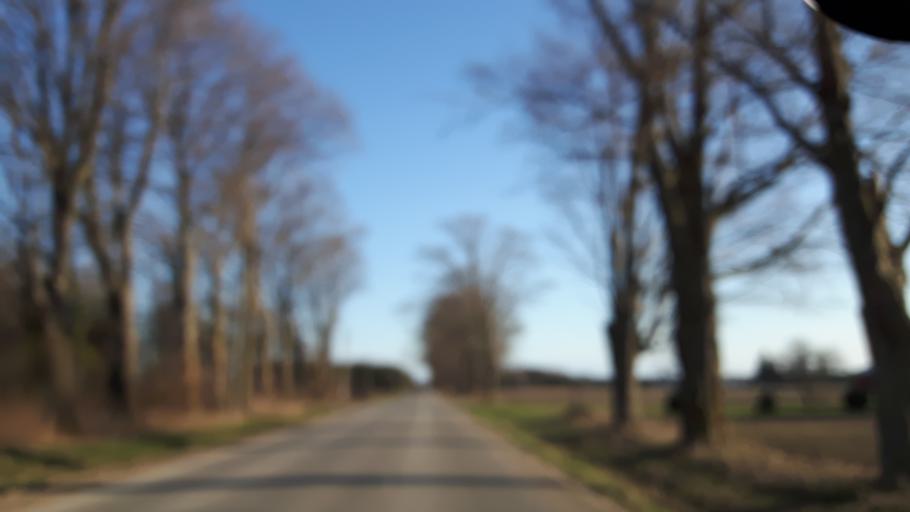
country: CA
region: Ontario
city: Goderich
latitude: 43.6942
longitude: -81.6849
